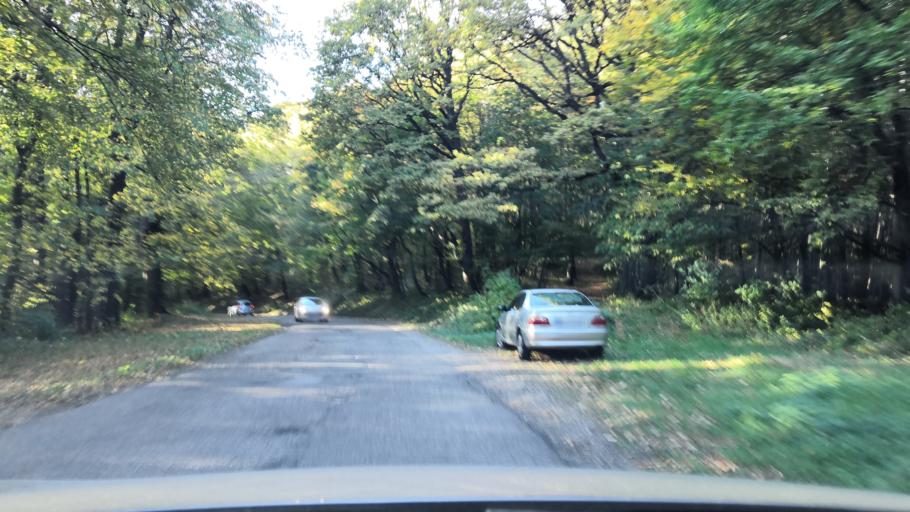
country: RS
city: Vrdnik
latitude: 45.1587
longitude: 19.7859
